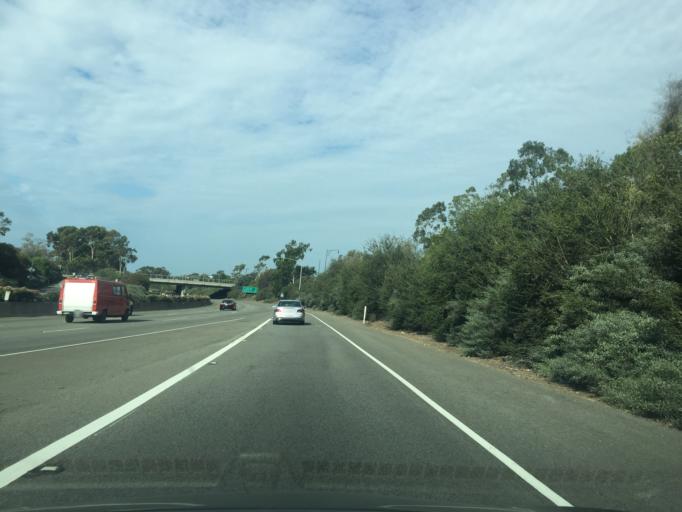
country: US
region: California
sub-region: Santa Barbara County
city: Mission Canyon
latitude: 34.4410
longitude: -119.7566
